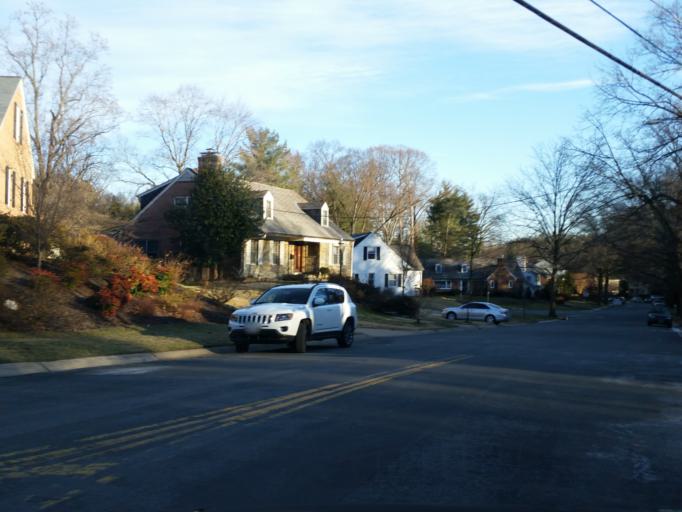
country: US
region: Maryland
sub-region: Montgomery County
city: Brookmont
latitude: 38.9542
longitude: -77.1190
